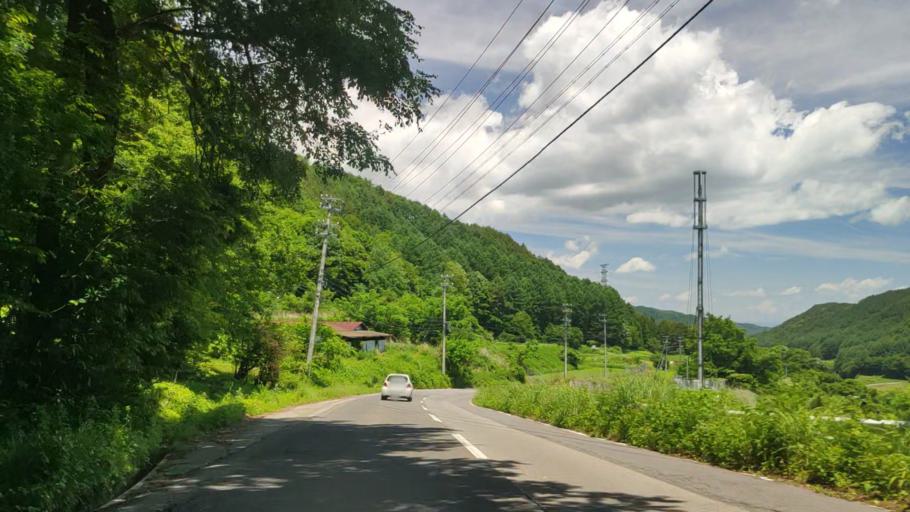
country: JP
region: Nagano
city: Kamimaruko
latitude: 36.1818
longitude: 138.2442
